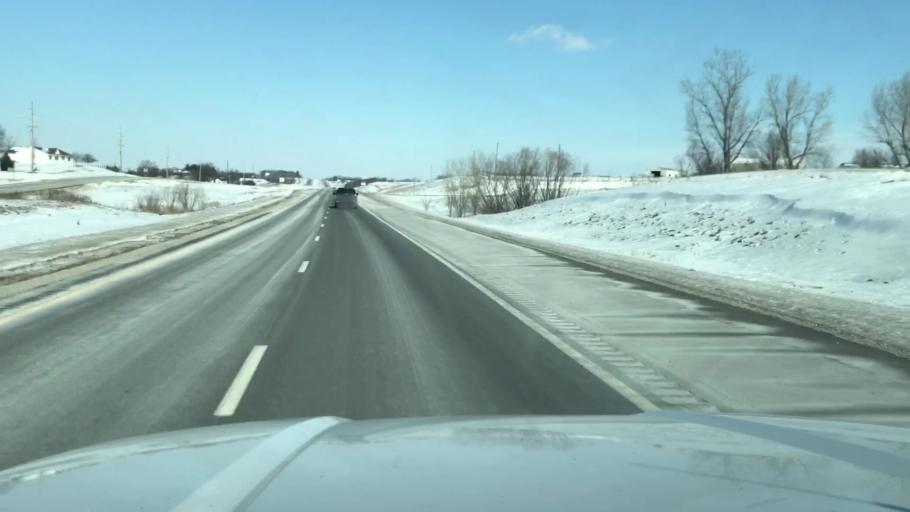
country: US
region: Missouri
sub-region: Nodaway County
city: Maryville
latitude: 40.1842
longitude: -94.8679
